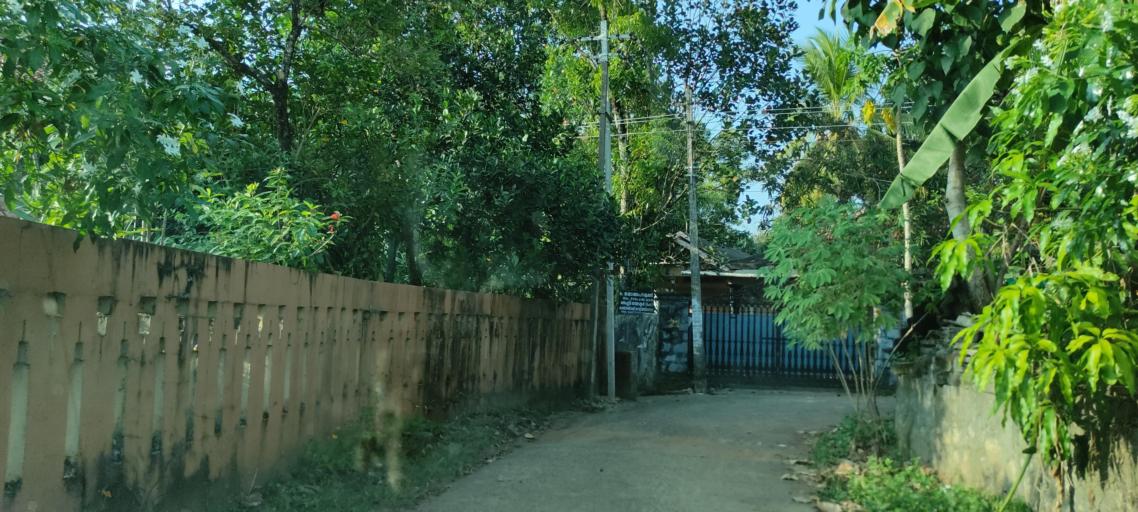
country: IN
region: Kerala
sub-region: Pattanamtitta
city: Adur
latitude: 9.1502
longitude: 76.7581
